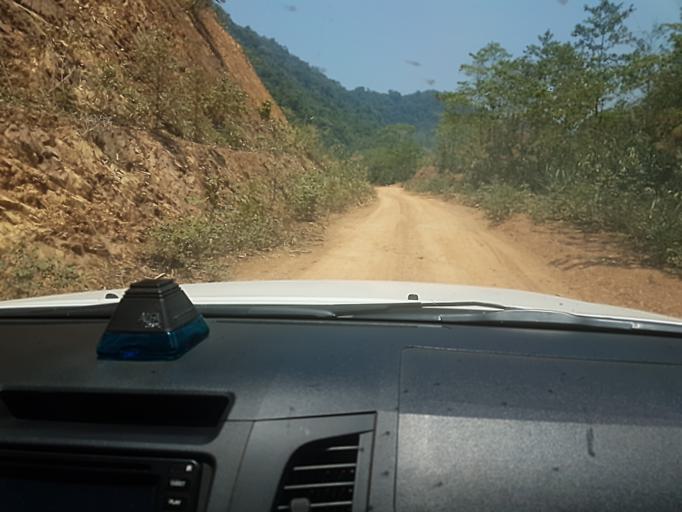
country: VN
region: Nghe An
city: Con Cuong
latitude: 18.6061
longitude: 104.7343
